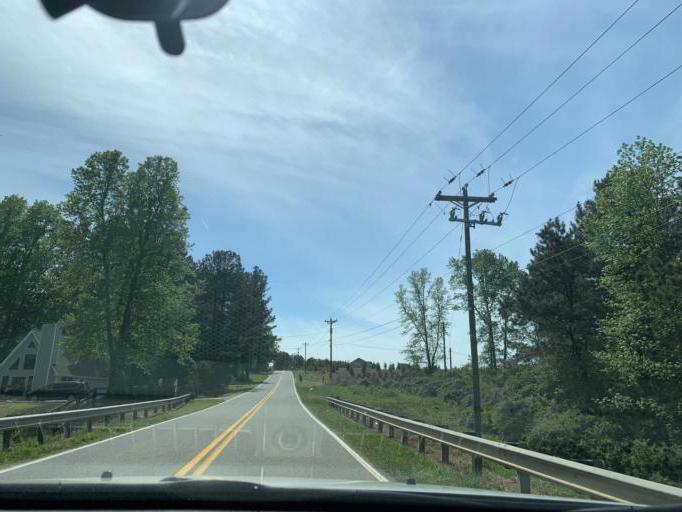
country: US
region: Georgia
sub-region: Forsyth County
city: Cumming
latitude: 34.2644
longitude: -84.1860
